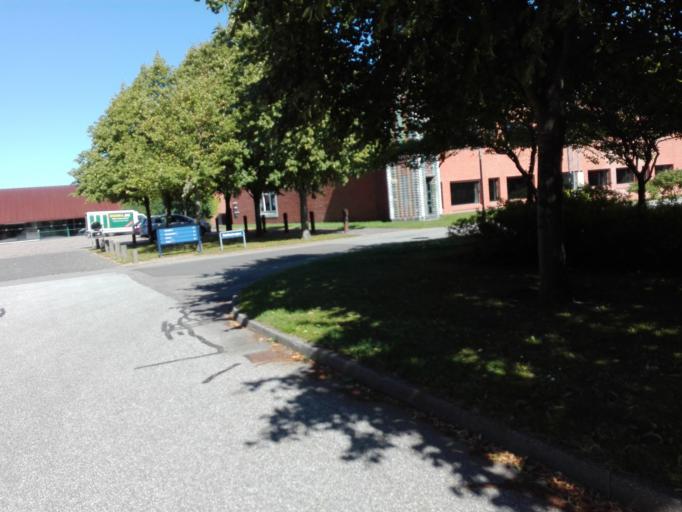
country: DK
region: Central Jutland
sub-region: Arhus Kommune
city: Tranbjerg
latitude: 56.1070
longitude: 10.1392
